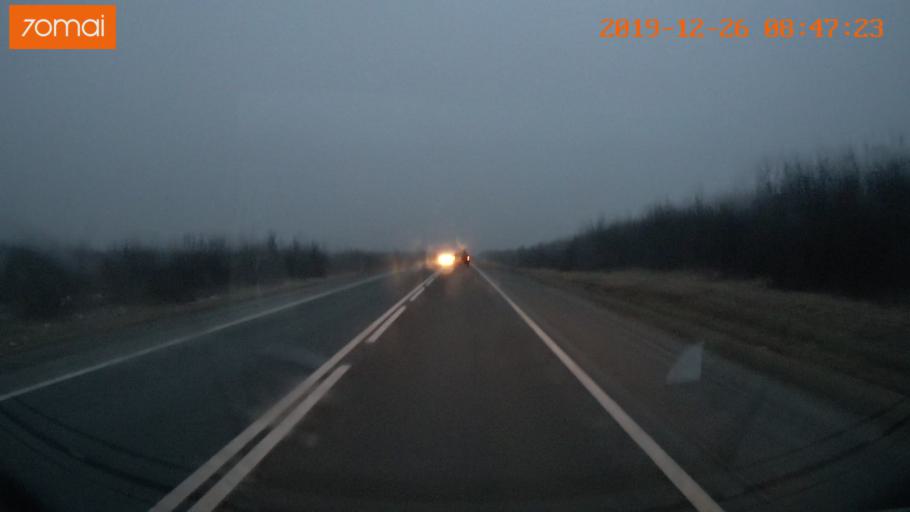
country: RU
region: Jaroslavl
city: Prechistoye
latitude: 58.6221
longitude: 40.3319
